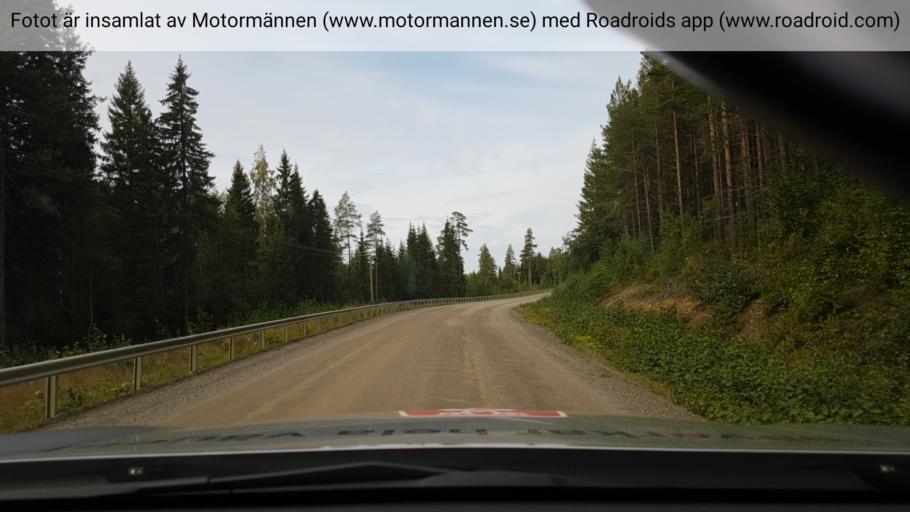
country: SE
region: Vaesterbotten
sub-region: Bjurholms Kommun
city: Bjurholm
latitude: 63.9184
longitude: 19.3779
